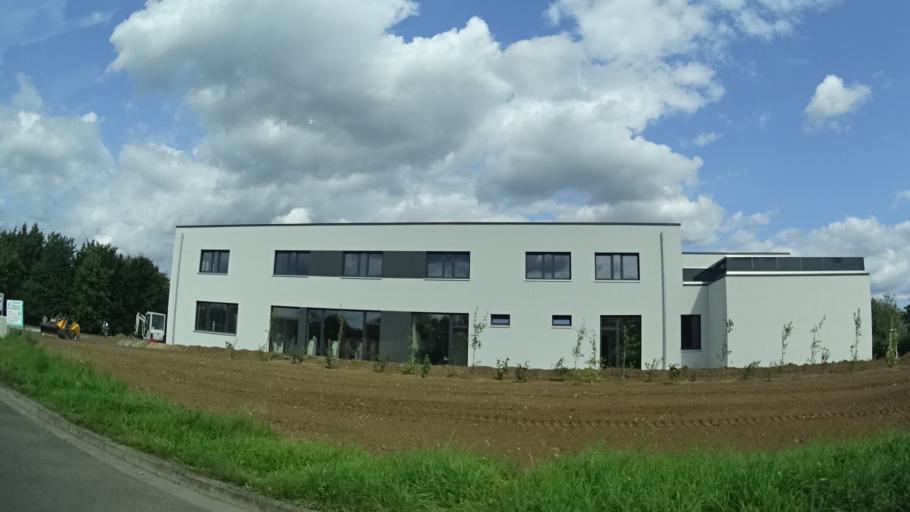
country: DE
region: Bavaria
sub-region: Regierungsbezirk Unterfranken
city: Grafenrheinfeld
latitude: 49.9958
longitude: 10.1986
